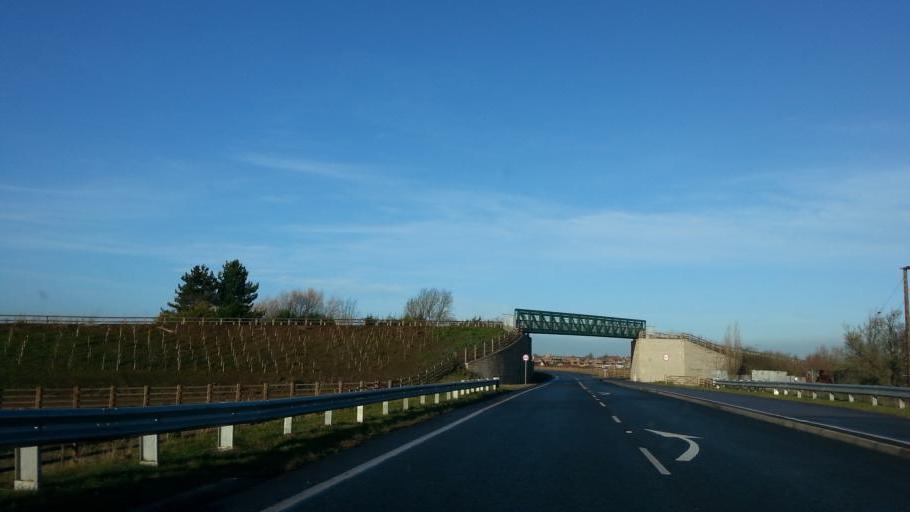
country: GB
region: England
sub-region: Nottinghamshire
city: Newark on Trent
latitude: 53.0499
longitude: -0.7993
